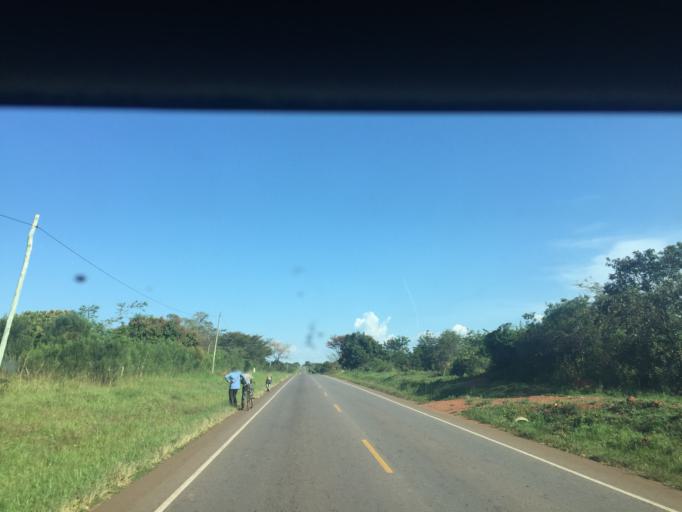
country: UG
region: Central Region
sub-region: Nakasongola District
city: Nakasongola
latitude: 1.3501
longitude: 32.3835
